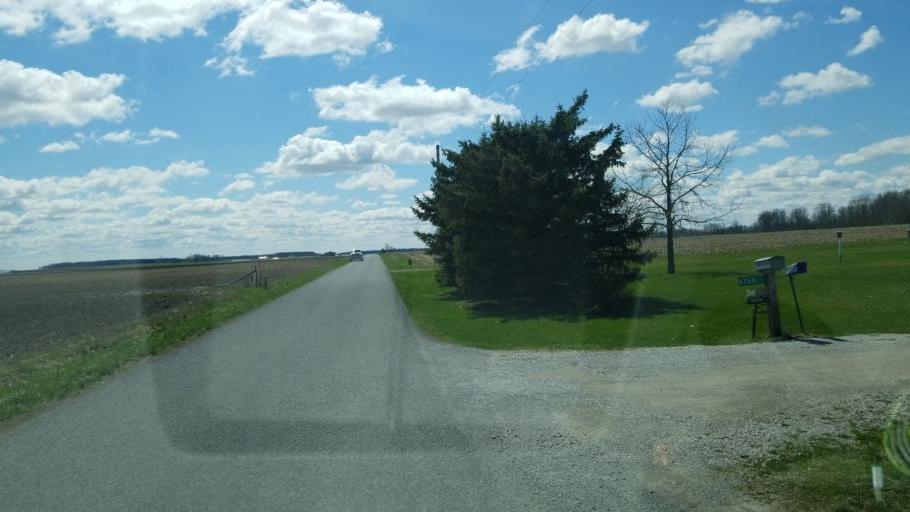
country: US
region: Ohio
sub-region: Seneca County
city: Fostoria
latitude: 41.0761
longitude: -83.5146
